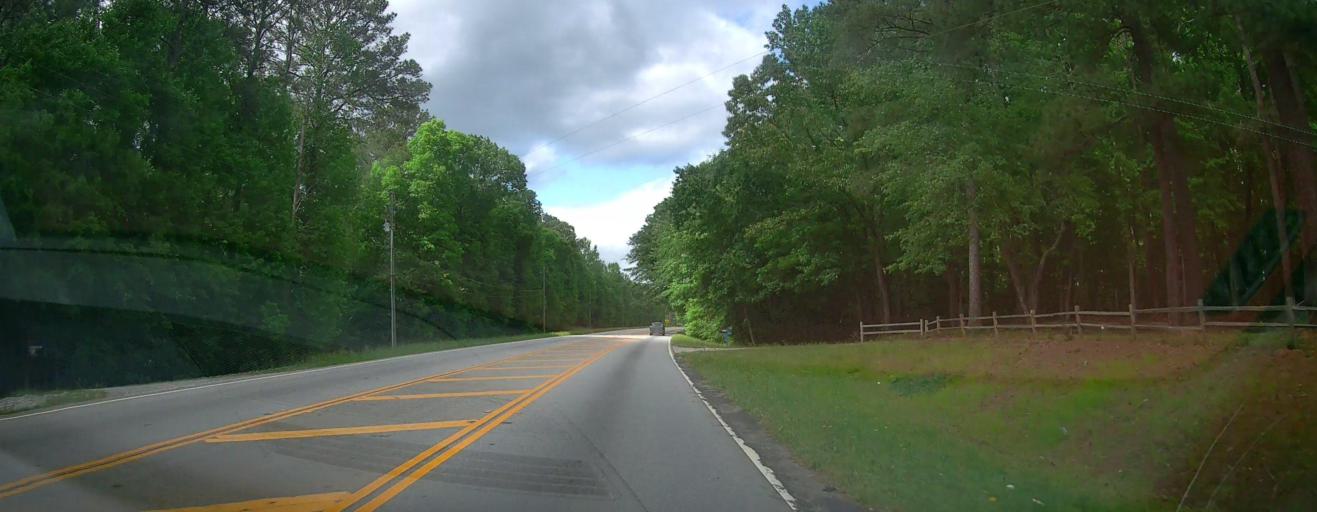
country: US
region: Georgia
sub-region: Walton County
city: Walnut Grove
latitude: 33.7153
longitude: -83.9290
